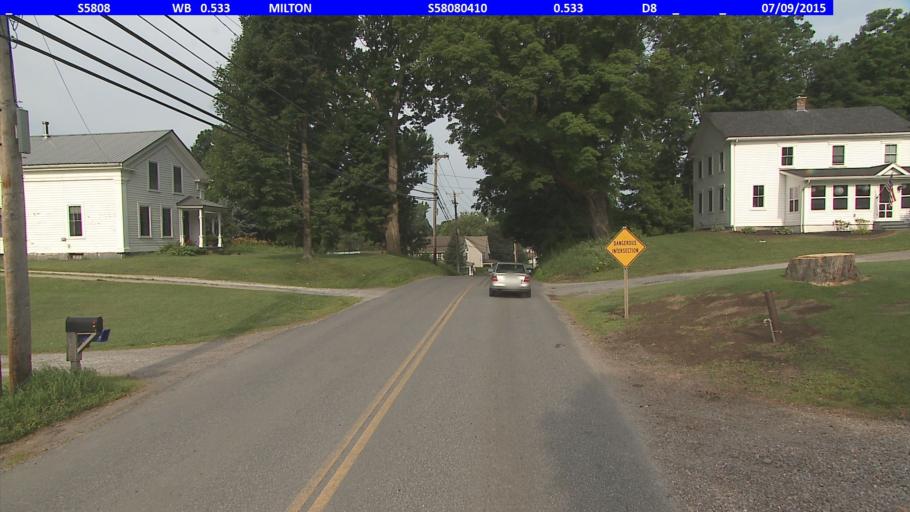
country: US
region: Vermont
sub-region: Chittenden County
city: Milton
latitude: 44.6387
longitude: -73.1030
